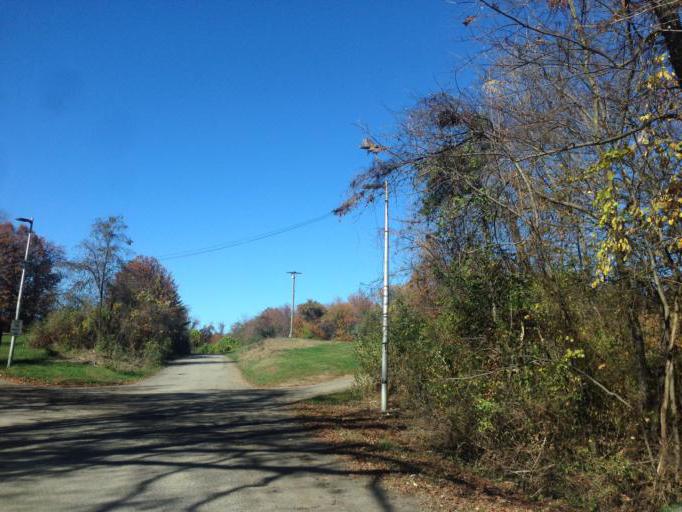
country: US
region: Maryland
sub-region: Howard County
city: Riverside
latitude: 39.2074
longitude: -76.8643
